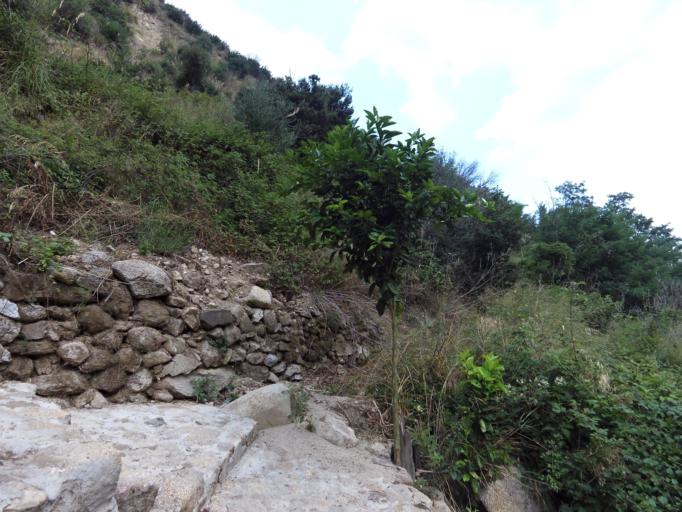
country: IT
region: Calabria
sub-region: Provincia di Reggio Calabria
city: Stilo
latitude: 38.4929
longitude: 16.4711
